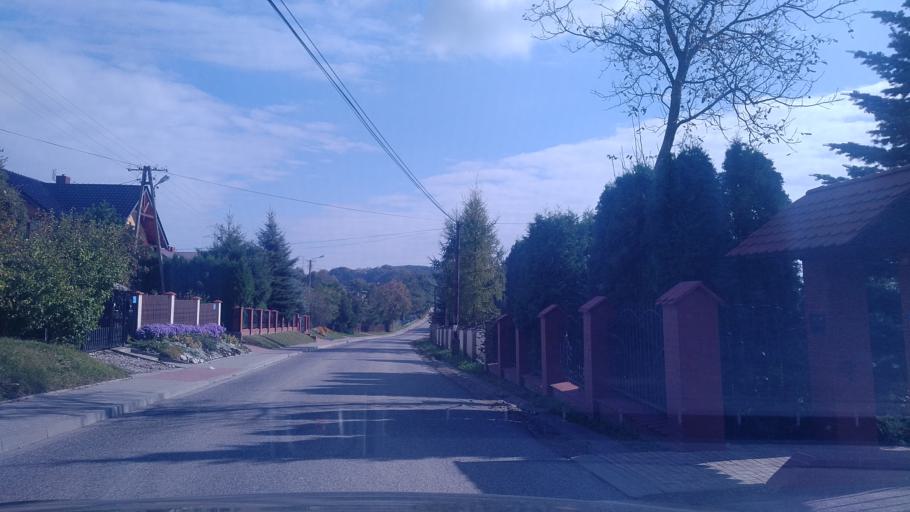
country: PL
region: Lesser Poland Voivodeship
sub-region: Powiat krakowski
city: Modlnica
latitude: 50.1349
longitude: 19.8501
